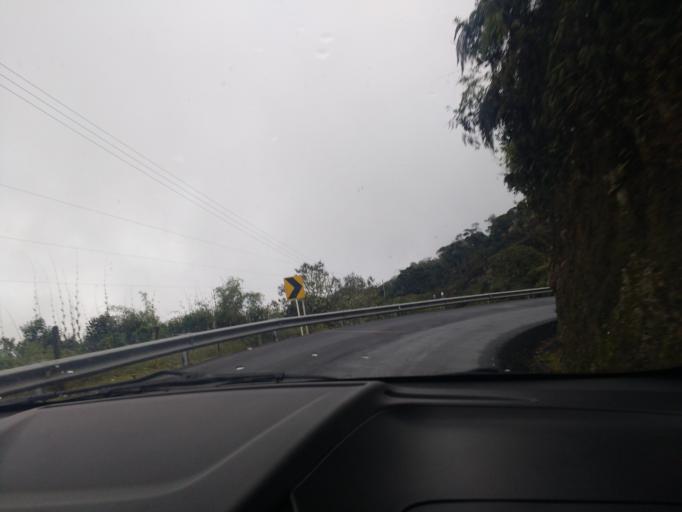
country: CO
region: Cundinamarca
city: Choachi
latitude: 4.5672
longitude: -73.9691
